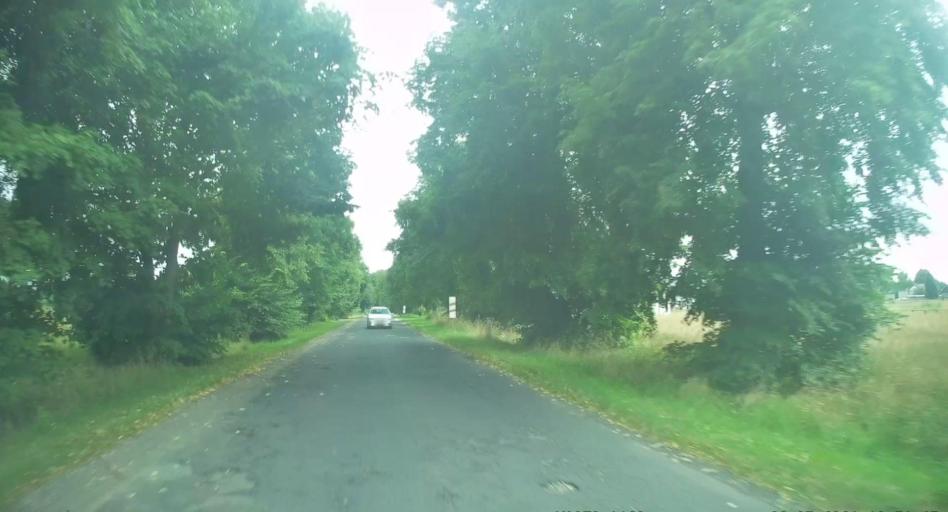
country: PL
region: Lodz Voivodeship
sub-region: Powiat rawski
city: Rawa Mazowiecka
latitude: 51.7513
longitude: 20.1880
